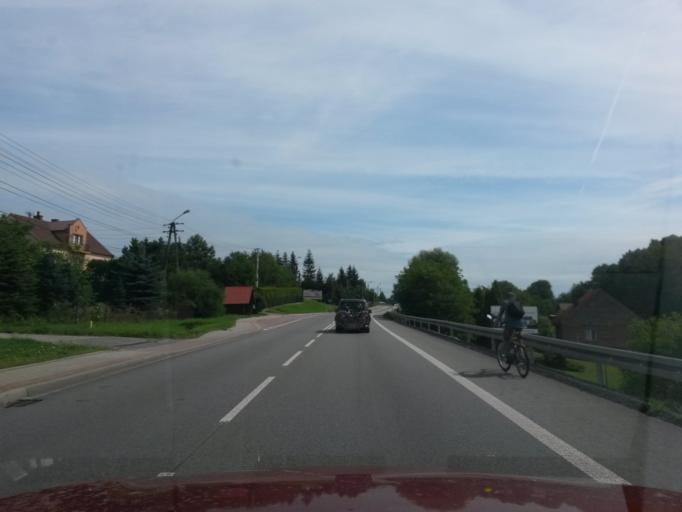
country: PL
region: Lesser Poland Voivodeship
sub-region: Powiat bochenski
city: Lapczyca
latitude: 49.9600
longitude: 20.3947
